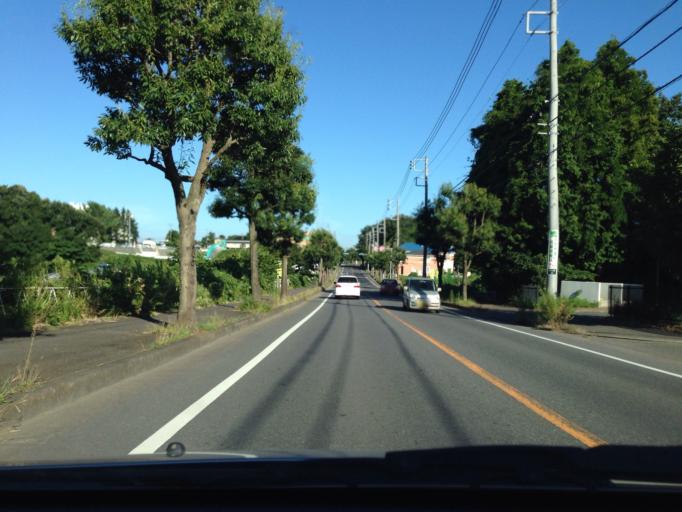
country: JP
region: Ibaraki
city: Naka
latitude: 36.0640
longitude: 140.1919
